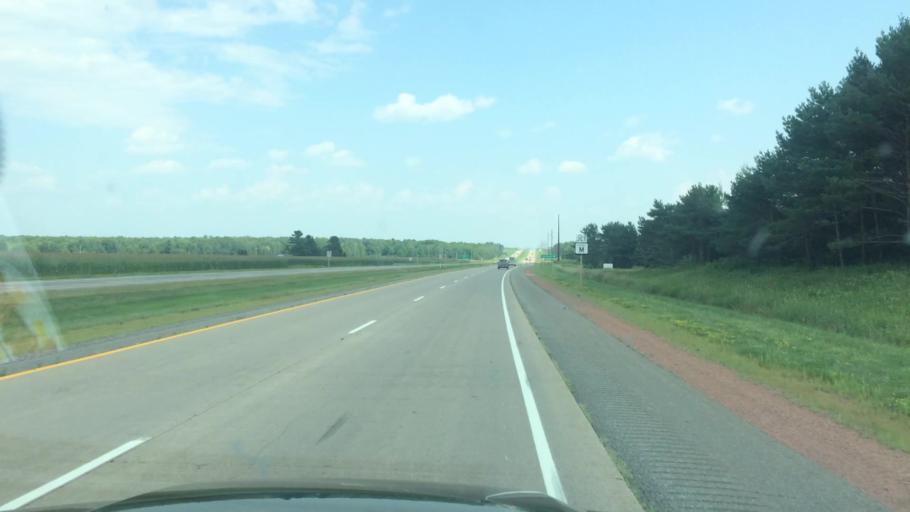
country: US
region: Wisconsin
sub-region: Marathon County
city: Edgar
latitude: 44.9440
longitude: -90.0298
